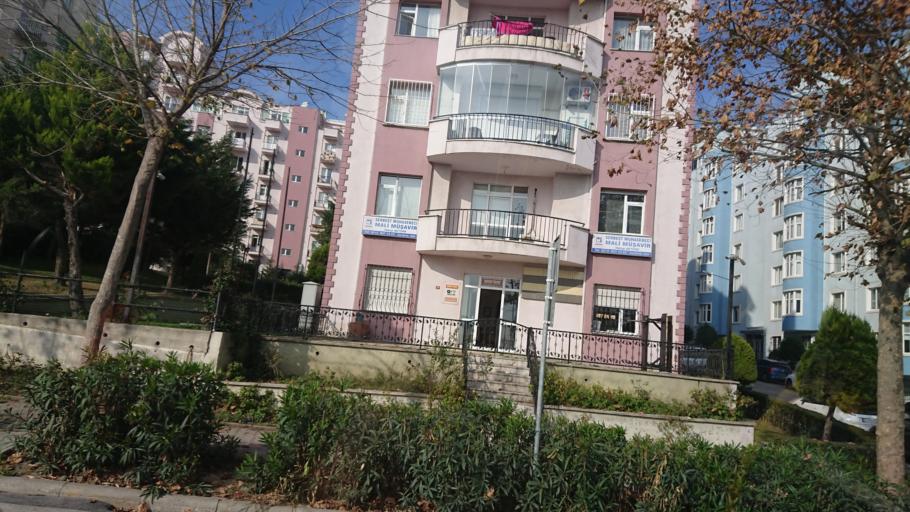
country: TR
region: Istanbul
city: Esenyurt
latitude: 41.0734
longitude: 28.6672
